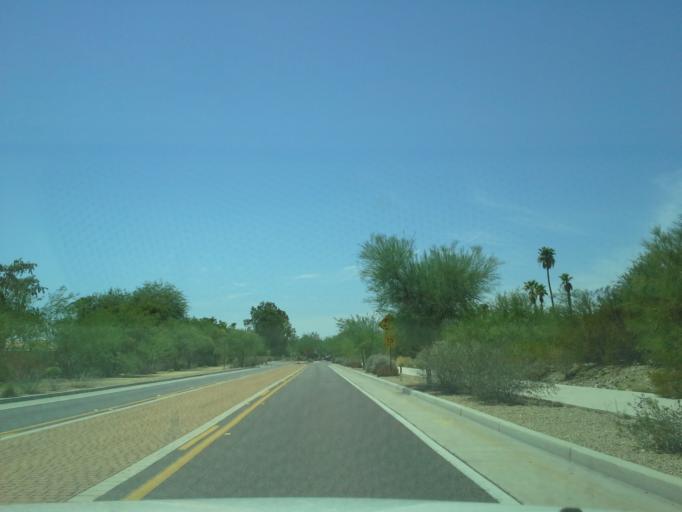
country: US
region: Arizona
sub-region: Maricopa County
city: Scottsdale
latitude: 33.5970
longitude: -111.8547
